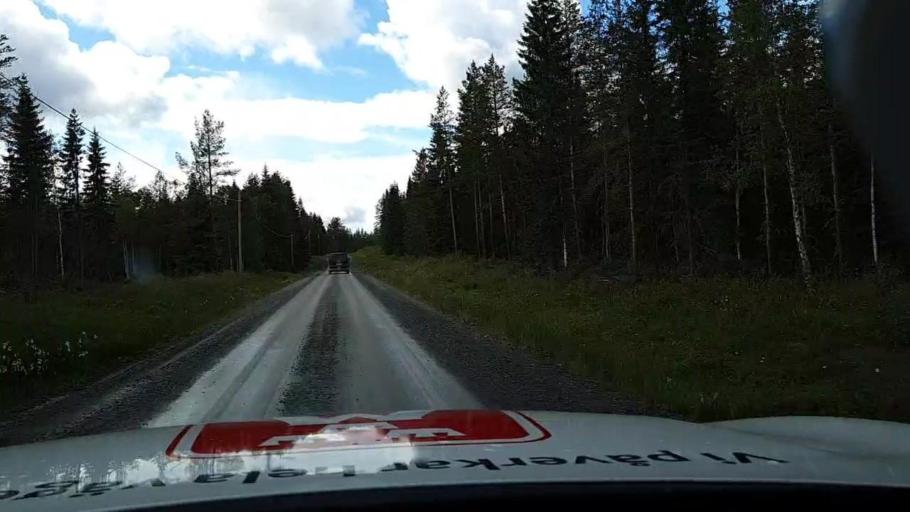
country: SE
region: Jaemtland
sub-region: Krokoms Kommun
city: Valla
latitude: 63.7085
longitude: 13.5559
